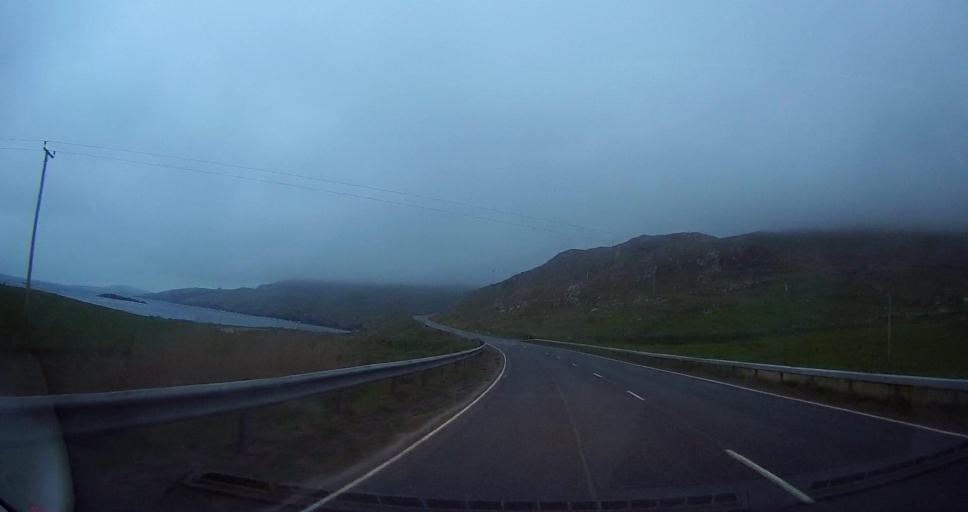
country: GB
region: Scotland
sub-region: Shetland Islands
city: Sandwick
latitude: 60.0354
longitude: -1.2319
